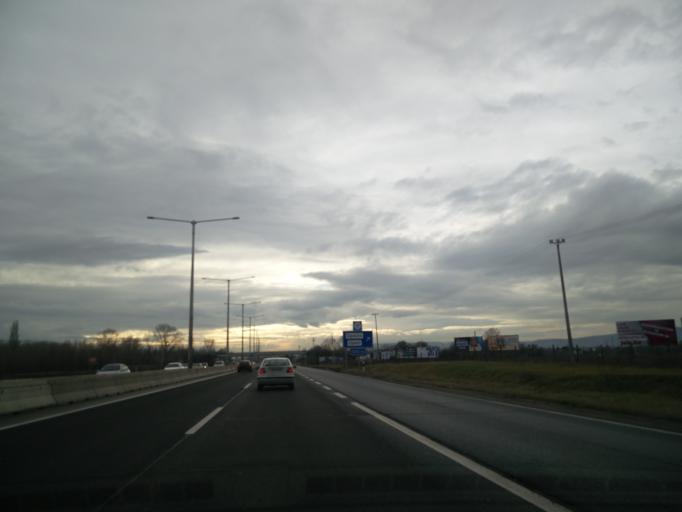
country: HU
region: Budapest
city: Budapest XV. keruelet
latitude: 47.5650
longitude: 19.1433
